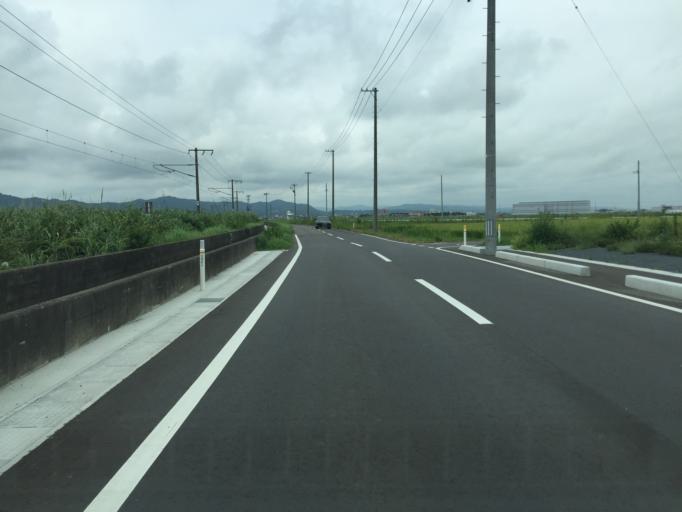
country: JP
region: Miyagi
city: Watari
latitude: 38.0228
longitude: 140.8800
